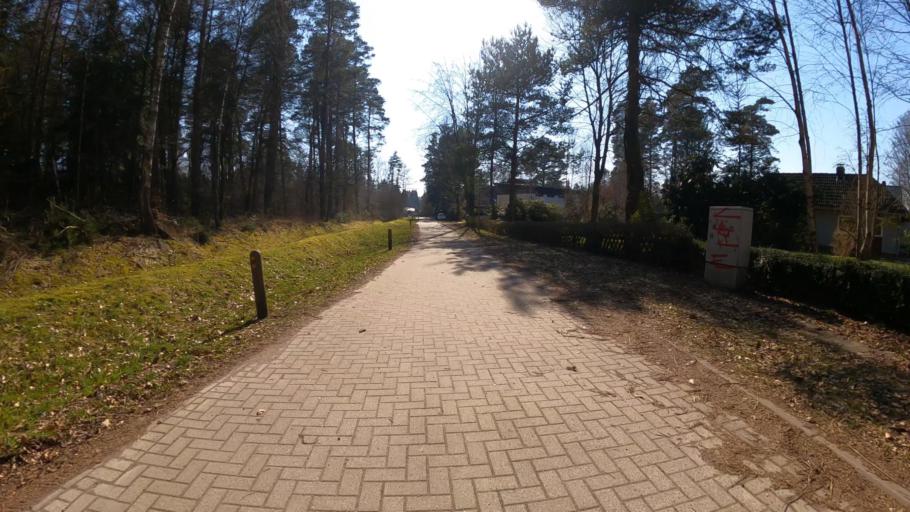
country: DE
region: Lower Saxony
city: Buchholz in der Nordheide
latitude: 53.3388
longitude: 9.9112
